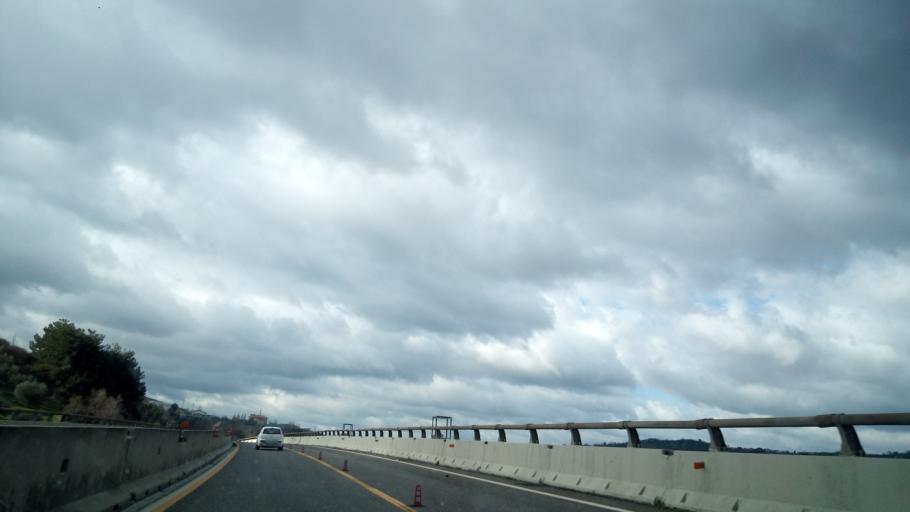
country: IT
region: Campania
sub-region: Provincia di Avellino
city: Flumeri
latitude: 41.0896
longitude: 15.1669
